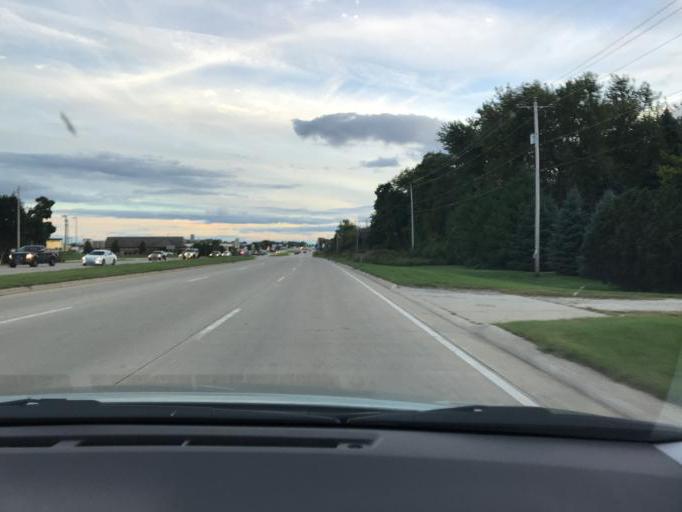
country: US
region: Wisconsin
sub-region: Kenosha County
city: Somers
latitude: 42.6026
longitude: -87.8792
